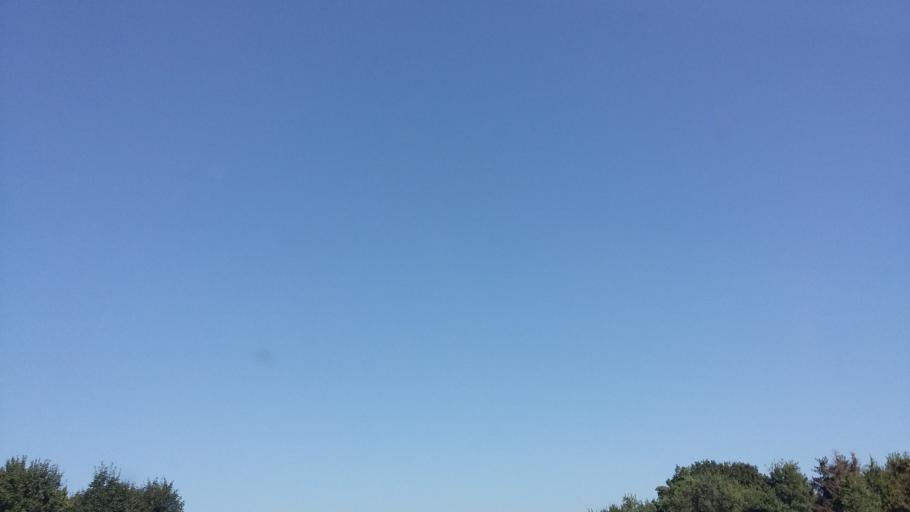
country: DE
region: Bavaria
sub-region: Swabia
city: Kleinaitingen
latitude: 48.1993
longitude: 10.8537
